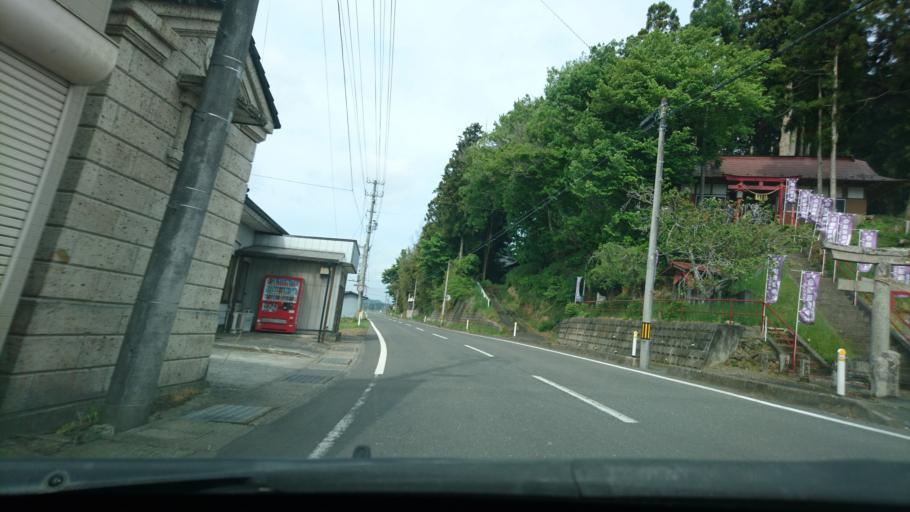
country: JP
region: Iwate
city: Ichinoseki
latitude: 38.8219
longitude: 141.0434
